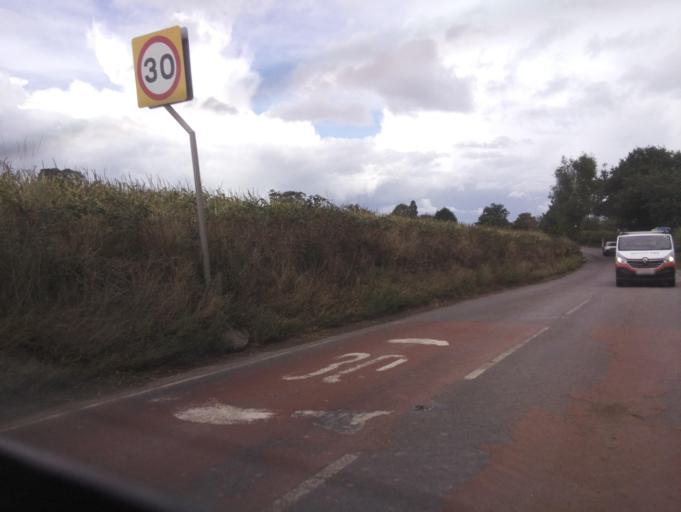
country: GB
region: England
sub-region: Telford and Wrekin
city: Newport
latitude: 52.7932
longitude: -2.3547
